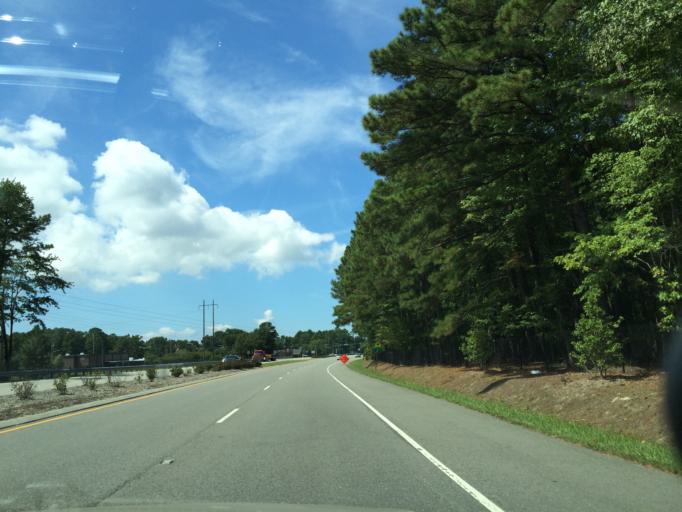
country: US
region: Virginia
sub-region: York County
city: Yorktown
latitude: 37.1772
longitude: -76.5236
